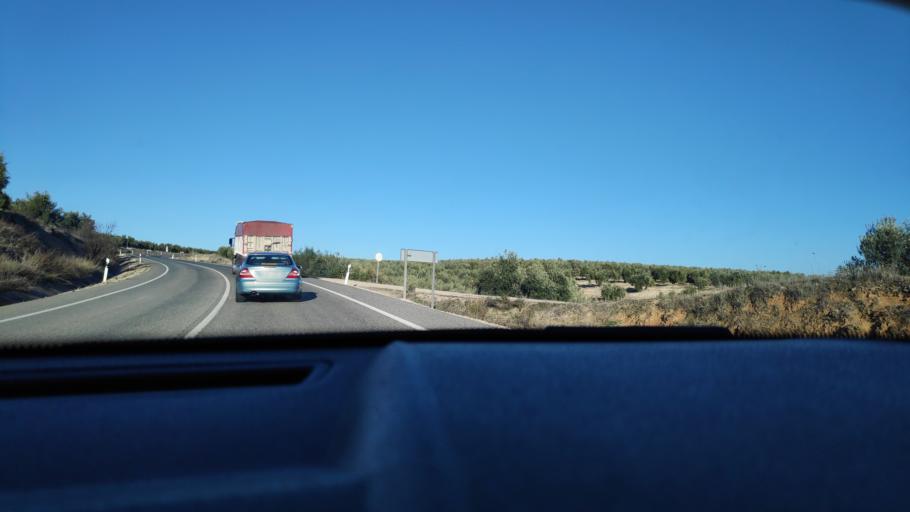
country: ES
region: Andalusia
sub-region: Provincia de Jaen
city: Martos
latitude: 37.6827
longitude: -4.0356
